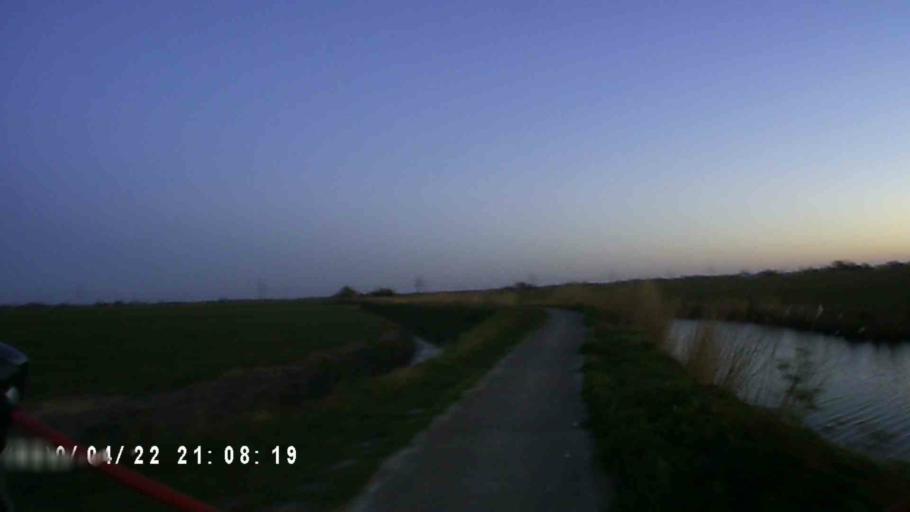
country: NL
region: Groningen
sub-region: Gemeente Winsum
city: Winsum
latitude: 53.3143
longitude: 6.5608
